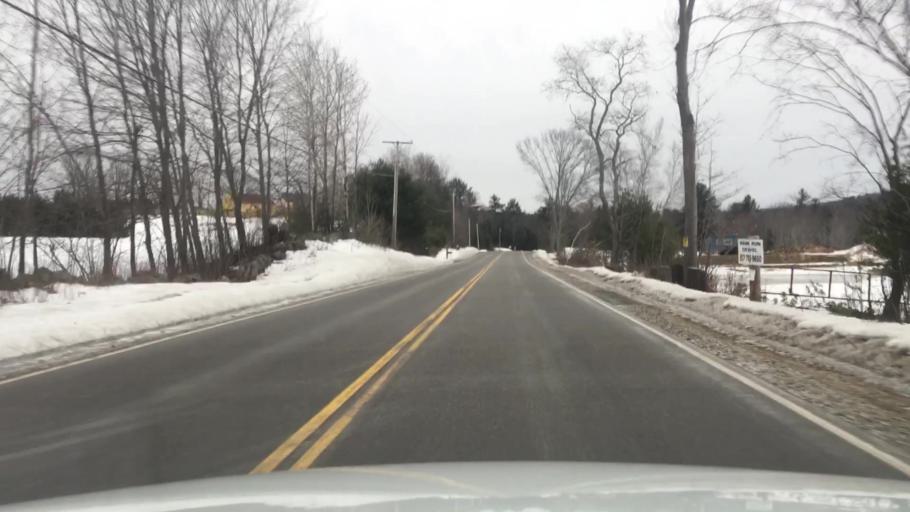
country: US
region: Maine
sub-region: York County
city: Limerick
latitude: 43.7151
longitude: -70.8136
